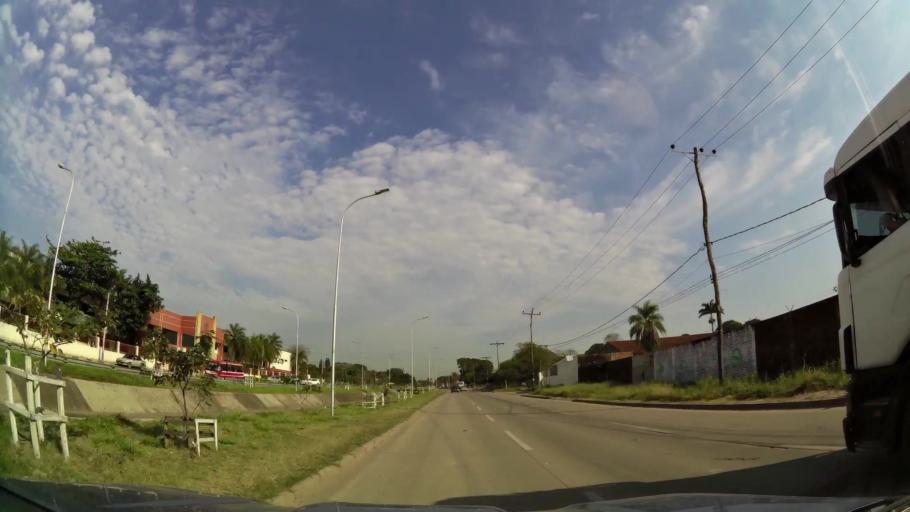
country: BO
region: Santa Cruz
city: Santa Cruz de la Sierra
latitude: -17.7347
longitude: -63.1607
